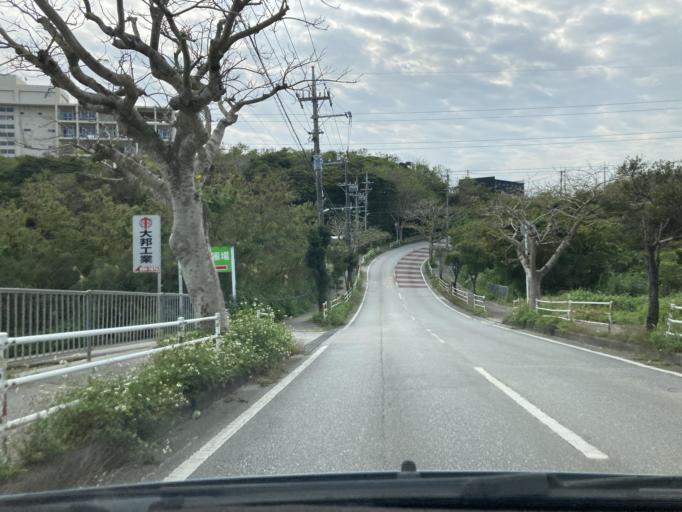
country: JP
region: Okinawa
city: Tomigusuku
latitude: 26.1846
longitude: 127.6950
